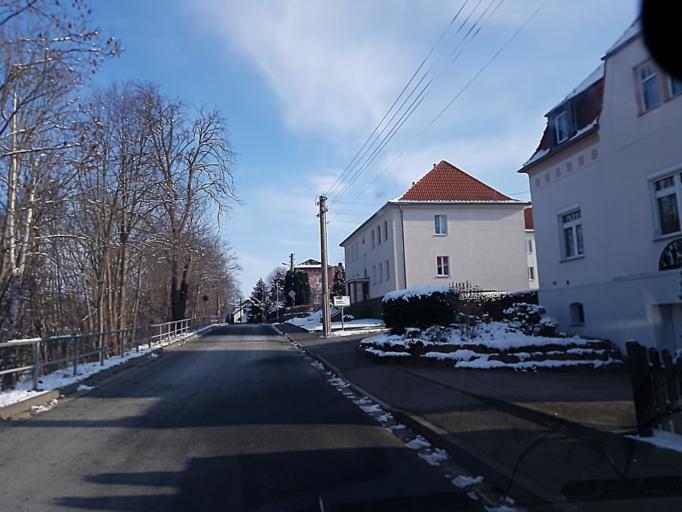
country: DE
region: Saxony
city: Leisnig
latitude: 51.1598
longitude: 12.9422
